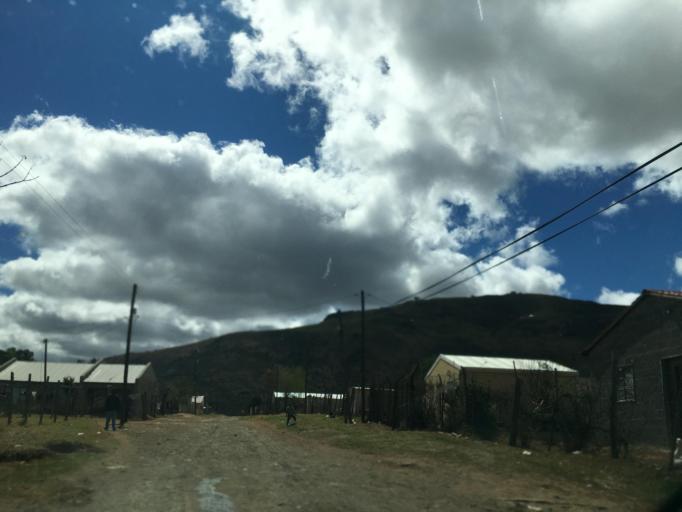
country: ZA
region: Eastern Cape
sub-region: Chris Hani District Municipality
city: Cala
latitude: -31.5315
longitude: 27.7025
